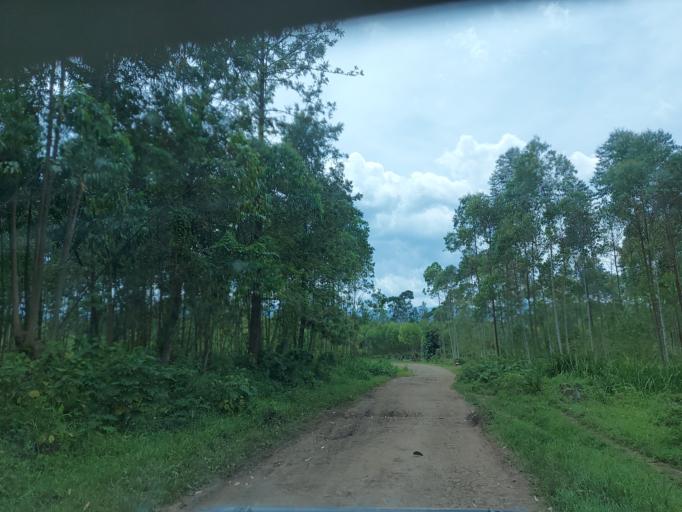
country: CD
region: South Kivu
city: Bukavu
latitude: -2.2443
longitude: 28.8251
